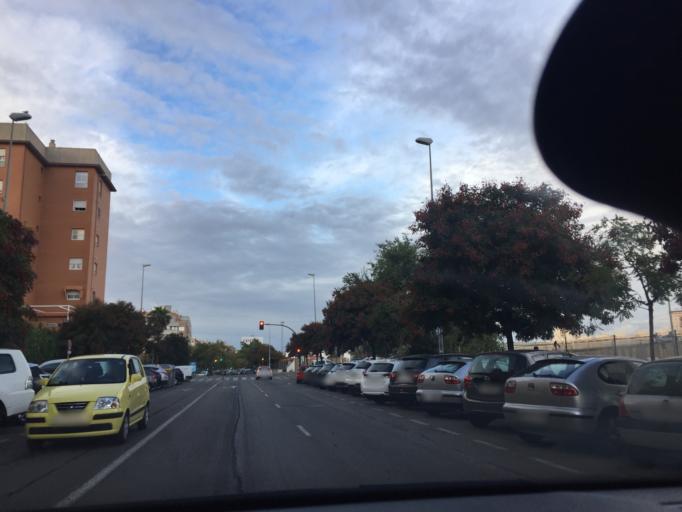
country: ES
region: Andalusia
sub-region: Provincia de Sevilla
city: Sevilla
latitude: 37.3948
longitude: -5.9744
